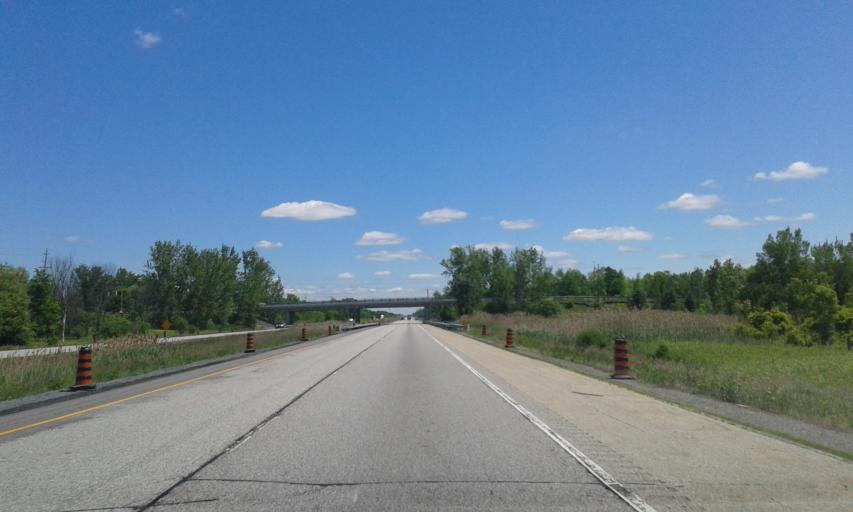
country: US
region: New York
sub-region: St. Lawrence County
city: Norfolk
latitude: 44.9370
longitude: -75.1504
